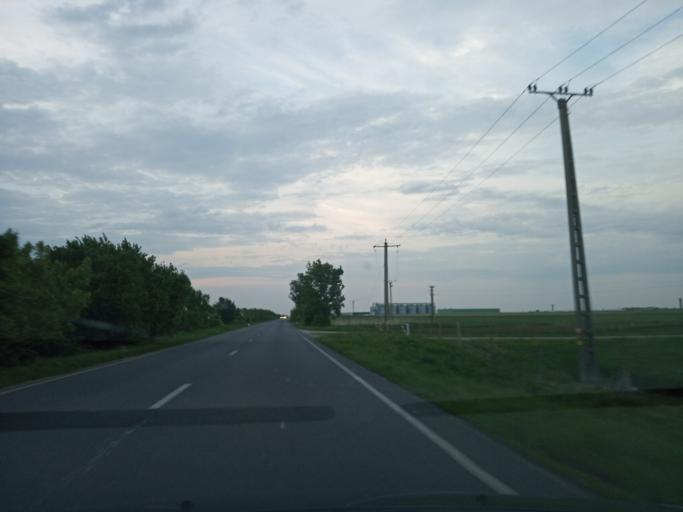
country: RO
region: Timis
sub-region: Comuna Voiteg
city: Voiteg
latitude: 45.4348
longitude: 21.2313
